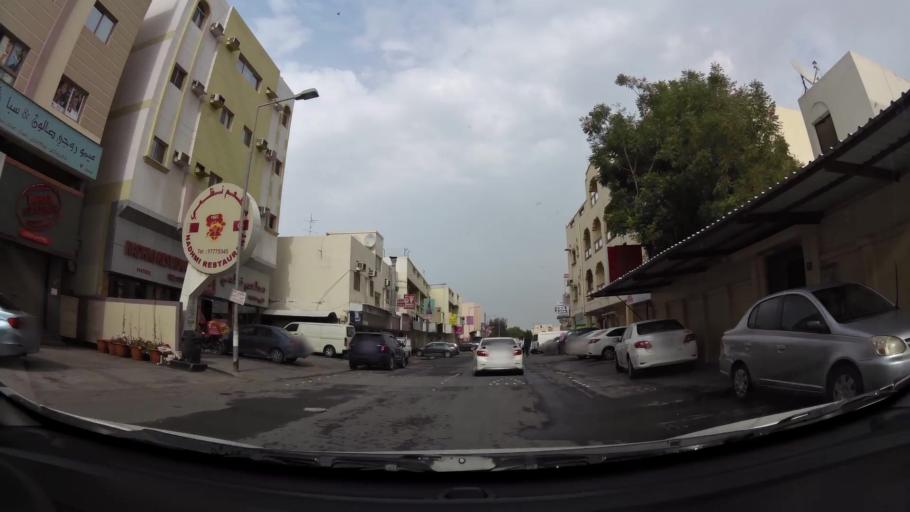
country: BH
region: Northern
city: Ar Rifa'
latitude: 26.1333
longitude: 50.5579
